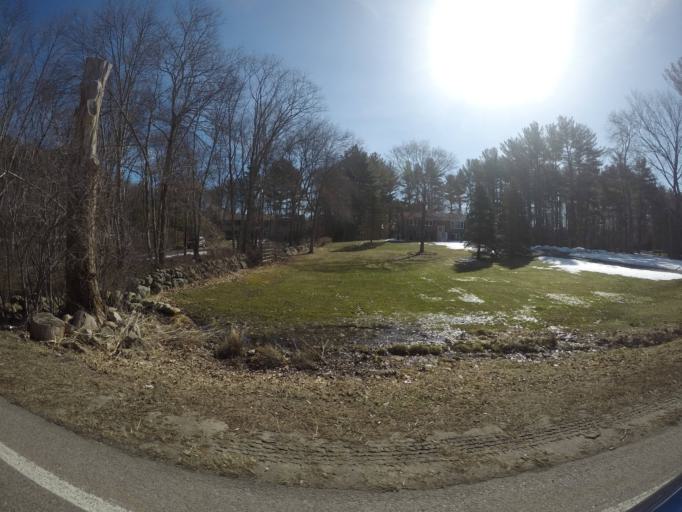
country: US
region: Massachusetts
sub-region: Bristol County
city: Easton
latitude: 42.0140
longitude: -71.1202
